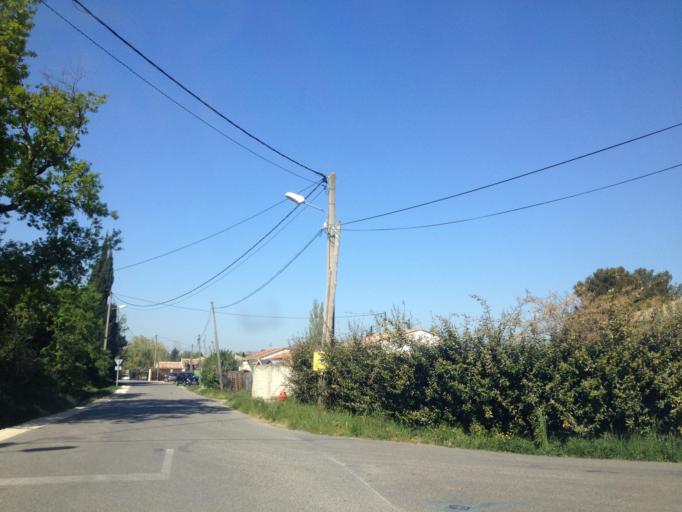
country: FR
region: Provence-Alpes-Cote d'Azur
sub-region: Departement du Vaucluse
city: Jonquieres
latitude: 44.1181
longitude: 4.8887
